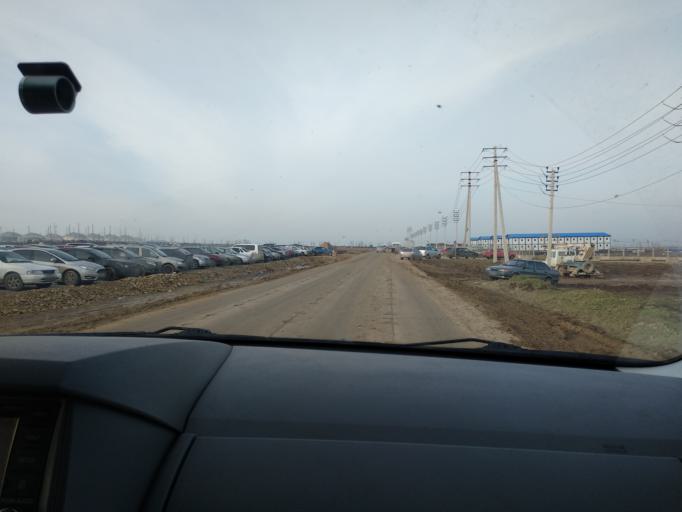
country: RU
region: Krasnodarskiy
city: Taman'
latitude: 45.1591
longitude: 36.6884
